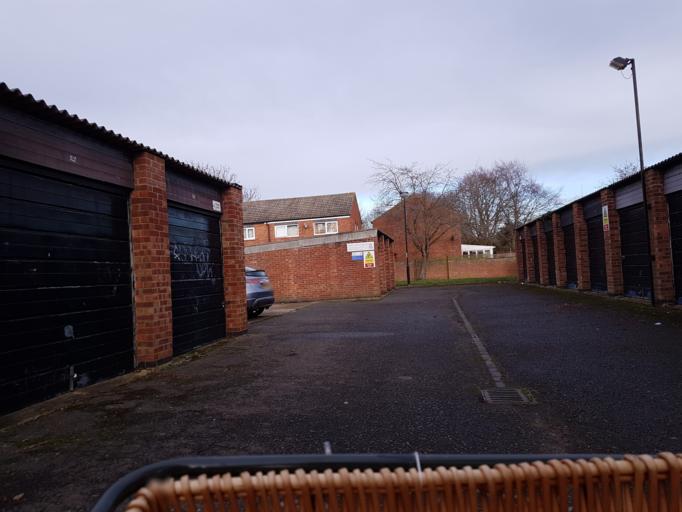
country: GB
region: England
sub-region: Cambridgeshire
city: Cambridge
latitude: 52.1902
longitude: 0.1472
